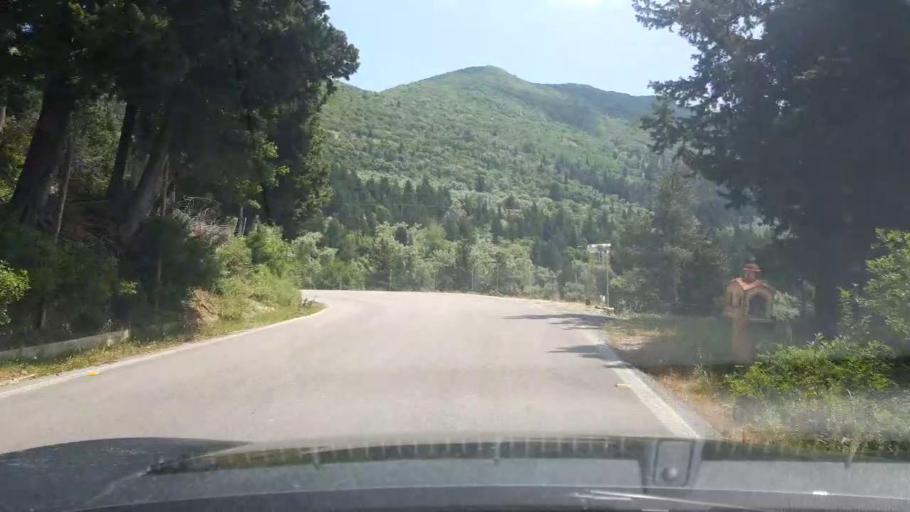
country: GR
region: Ionian Islands
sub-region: Lefkada
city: Nidri
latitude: 38.6527
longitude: 20.7059
